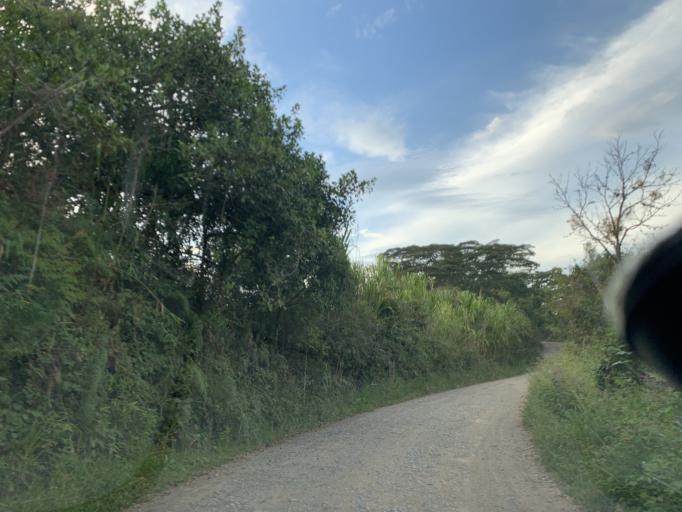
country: CO
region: Boyaca
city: Santana
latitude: 6.0755
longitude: -73.4866
